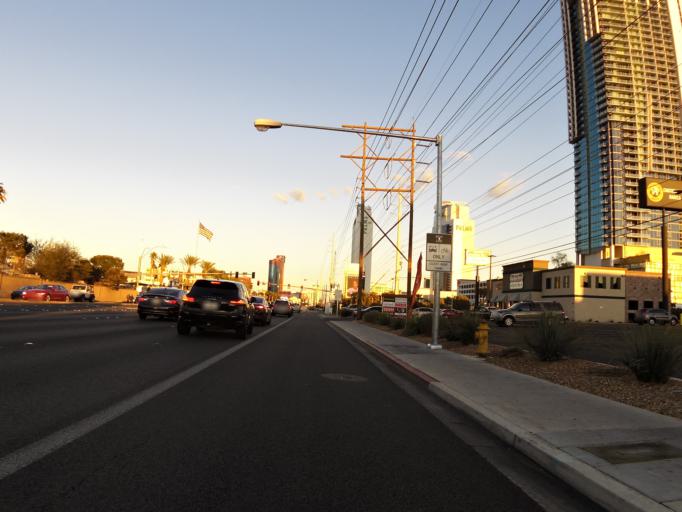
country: US
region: Nevada
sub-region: Clark County
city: Spring Valley
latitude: 36.1154
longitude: -115.2008
